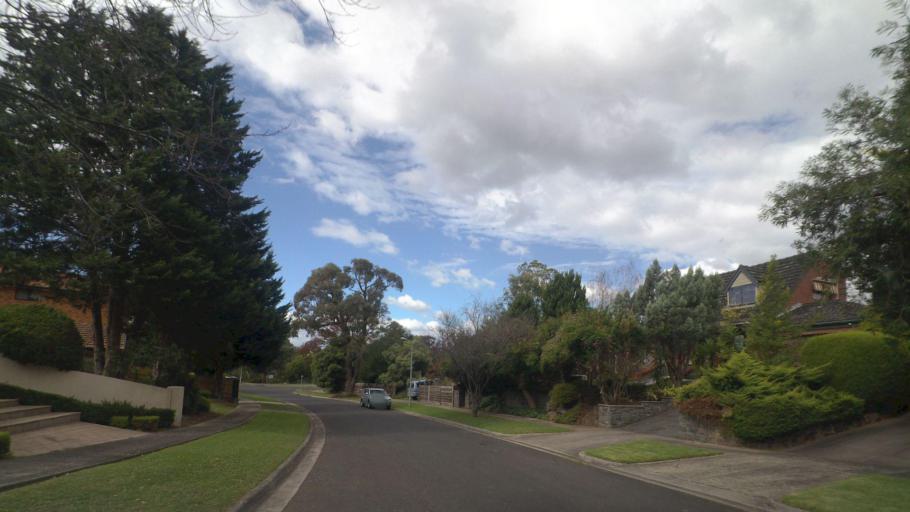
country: AU
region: Victoria
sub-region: Nillumbik
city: Eltham
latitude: -37.7571
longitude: 145.1571
